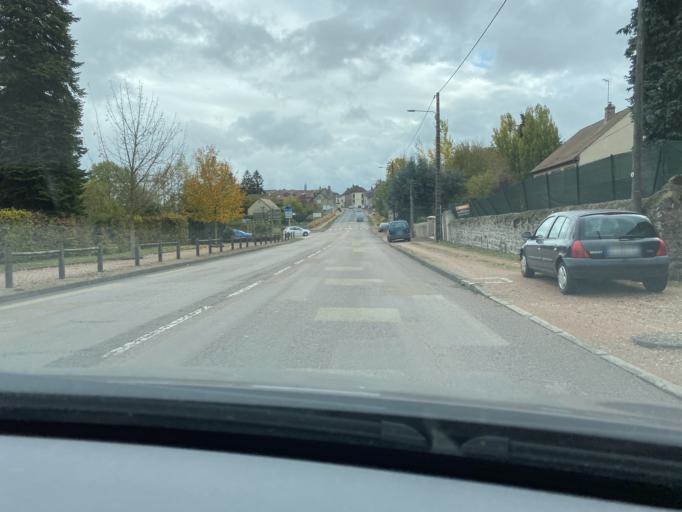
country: FR
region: Bourgogne
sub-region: Departement de la Cote-d'Or
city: Saulieu
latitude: 47.2850
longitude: 4.2262
